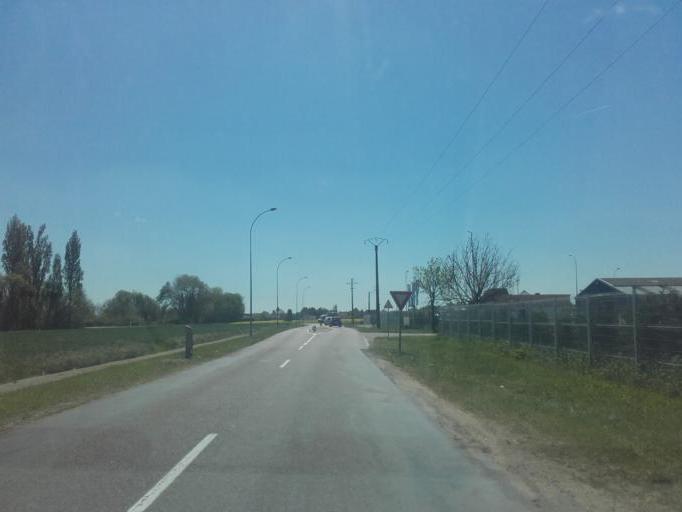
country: FR
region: Bourgogne
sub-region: Departement de la Cote-d'Or
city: Beaune
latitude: 47.0188
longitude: 4.8734
